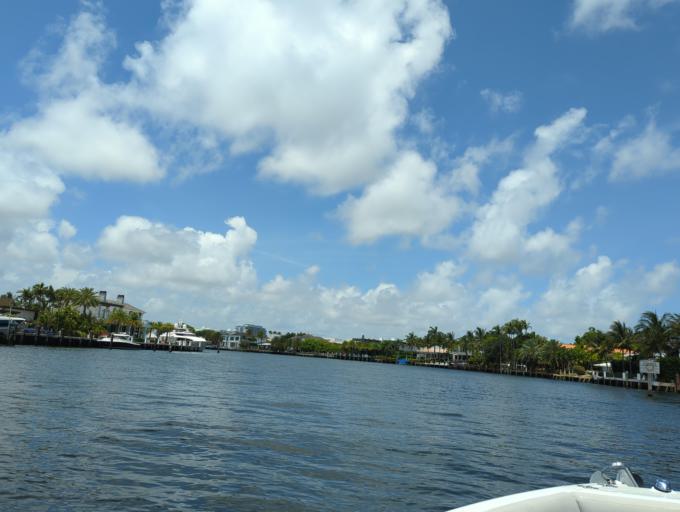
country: US
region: Florida
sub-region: Broward County
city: Sunrise
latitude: 26.1301
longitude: -80.1125
